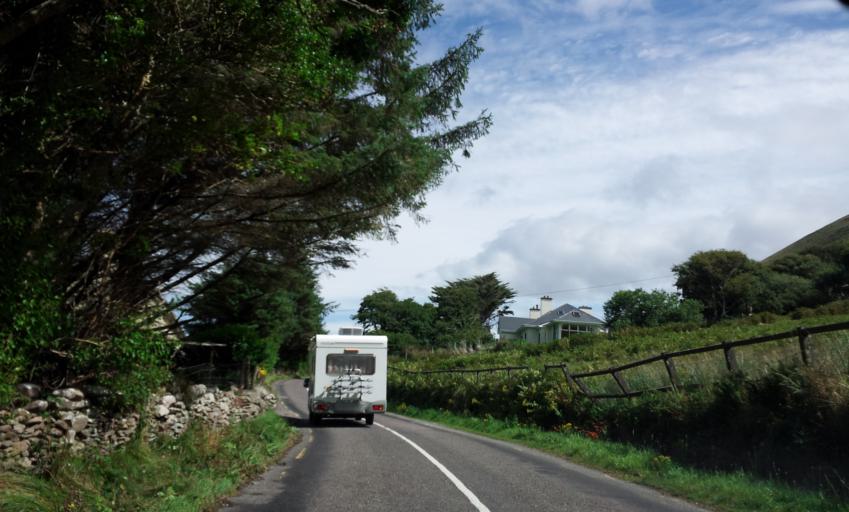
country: IE
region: Munster
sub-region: Ciarrai
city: Killorglin
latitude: 52.0550
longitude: -9.9666
